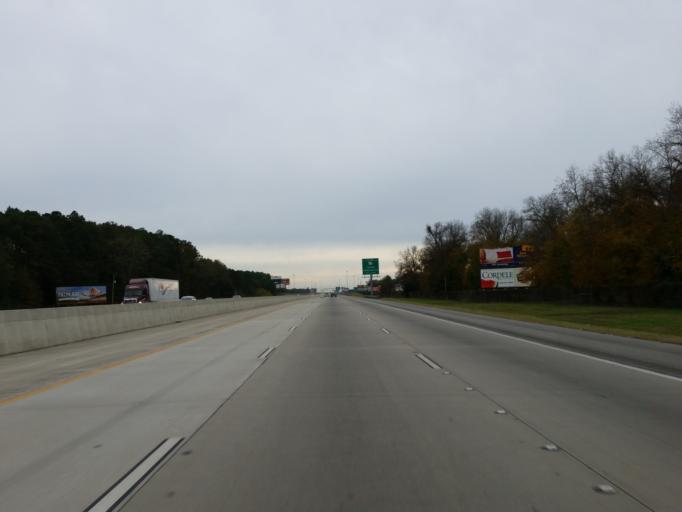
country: US
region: Georgia
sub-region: Crisp County
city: Cordele
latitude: 31.9896
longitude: -83.7563
